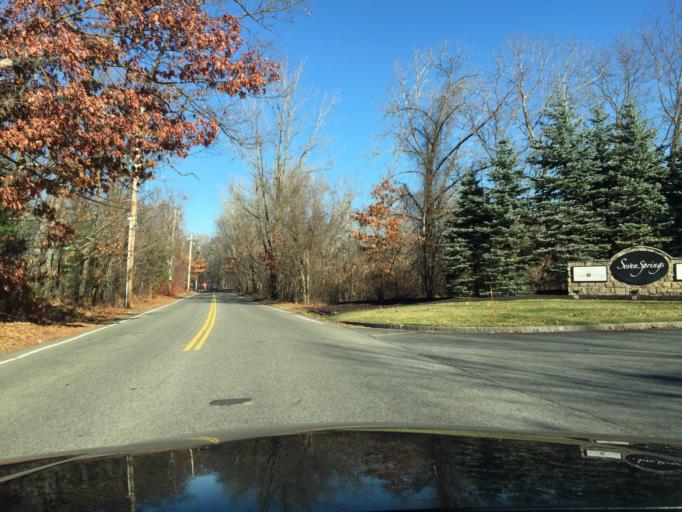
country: US
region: Massachusetts
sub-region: Middlesex County
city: Burlington
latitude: 42.4767
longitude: -71.2097
